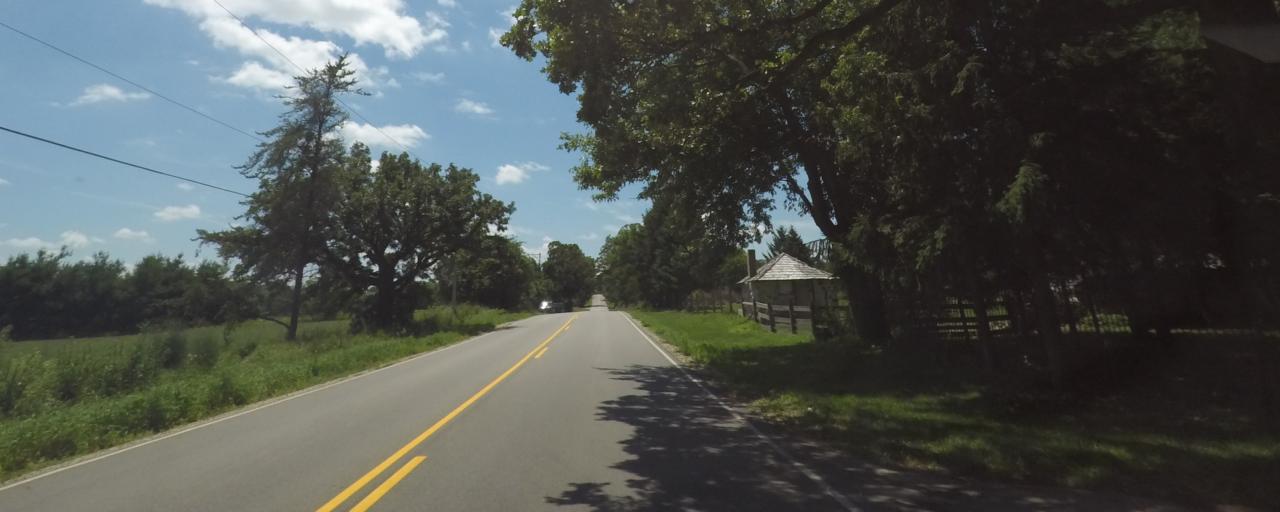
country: US
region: Wisconsin
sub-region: Waukesha County
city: Dousman
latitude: 42.9675
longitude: -88.4605
